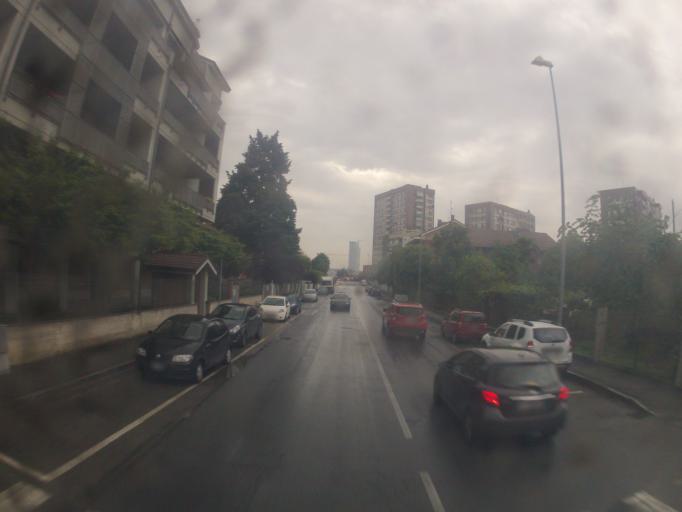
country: IT
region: Piedmont
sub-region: Provincia di Torino
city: Moncalieri
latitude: 45.0055
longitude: 7.6696
